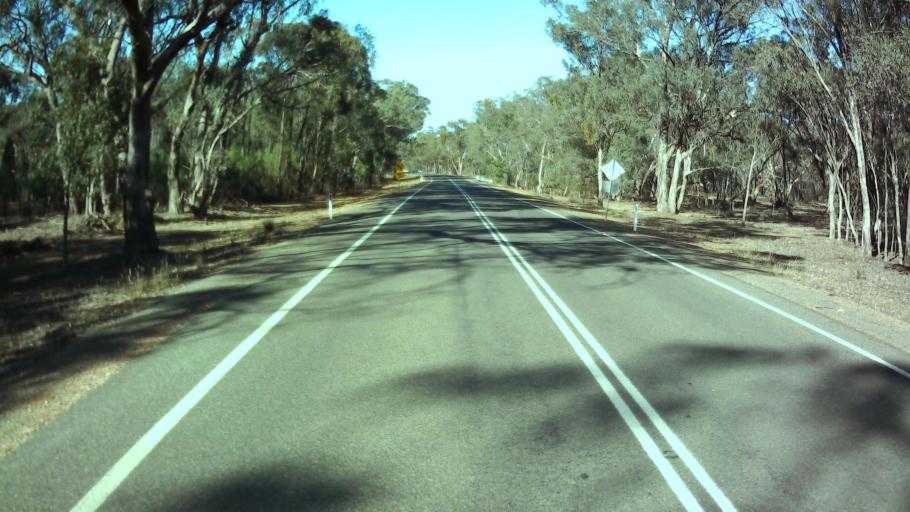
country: AU
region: New South Wales
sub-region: Weddin
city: Grenfell
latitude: -34.0015
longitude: 148.1287
